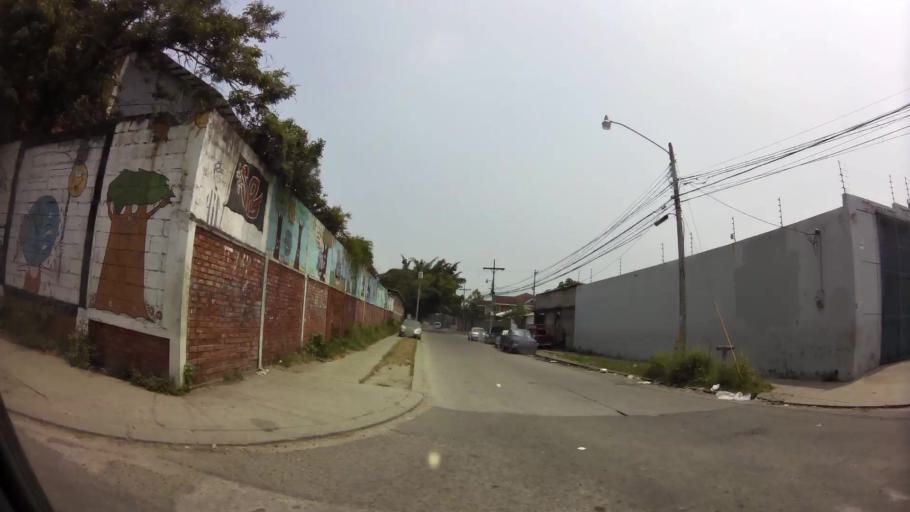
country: HN
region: Cortes
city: San Pedro Sula
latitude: 15.4918
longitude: -87.9981
